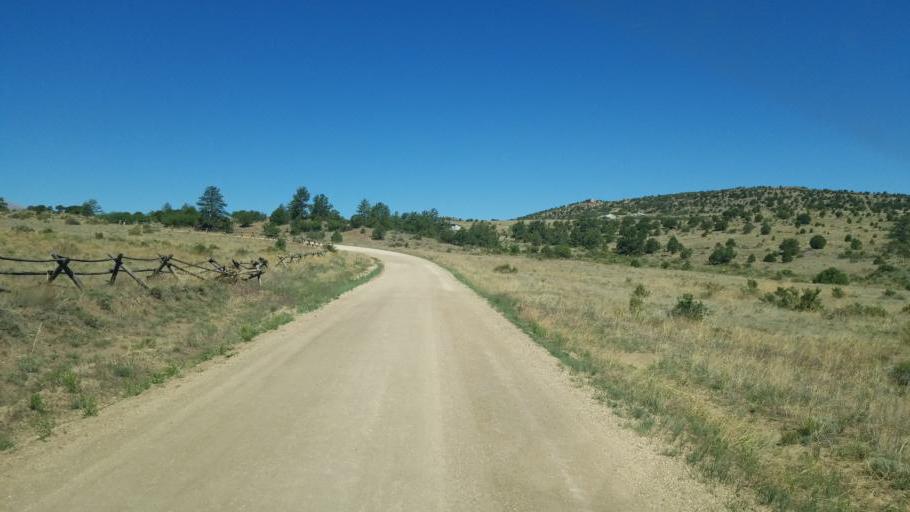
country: US
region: Colorado
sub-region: Custer County
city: Westcliffe
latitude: 38.2366
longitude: -105.4808
